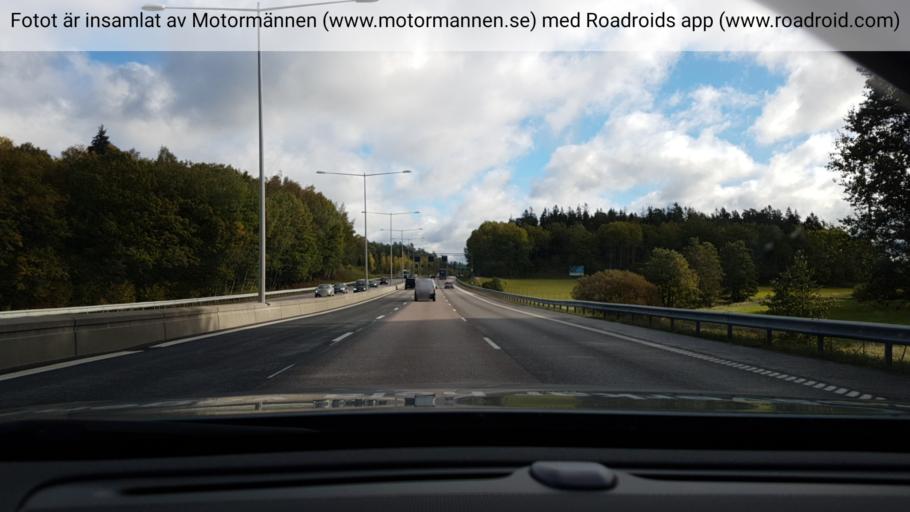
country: SE
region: Stockholm
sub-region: Salems Kommun
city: Ronninge
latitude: 59.2110
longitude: 17.7418
